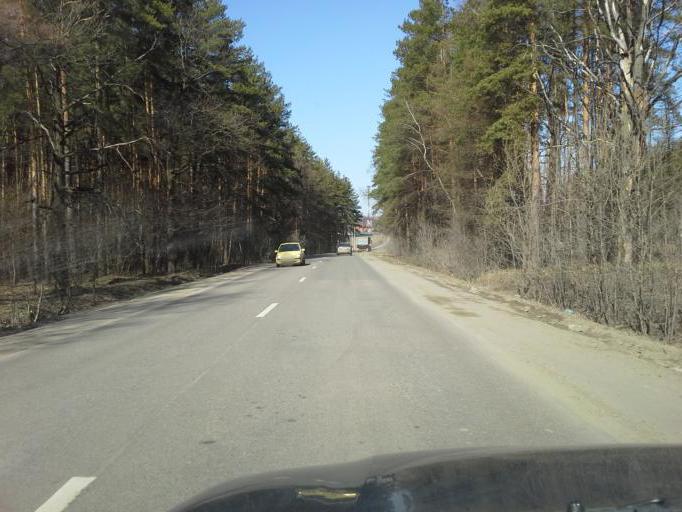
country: RU
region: Moskovskaya
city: Kokoshkino
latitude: 55.6078
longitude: 37.1643
